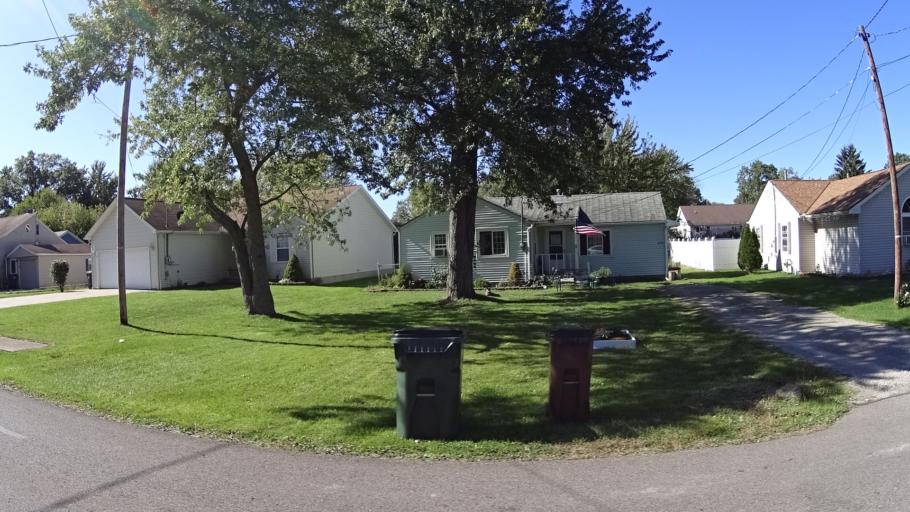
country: US
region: Ohio
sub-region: Lorain County
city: Lorain
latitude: 41.4243
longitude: -82.1577
